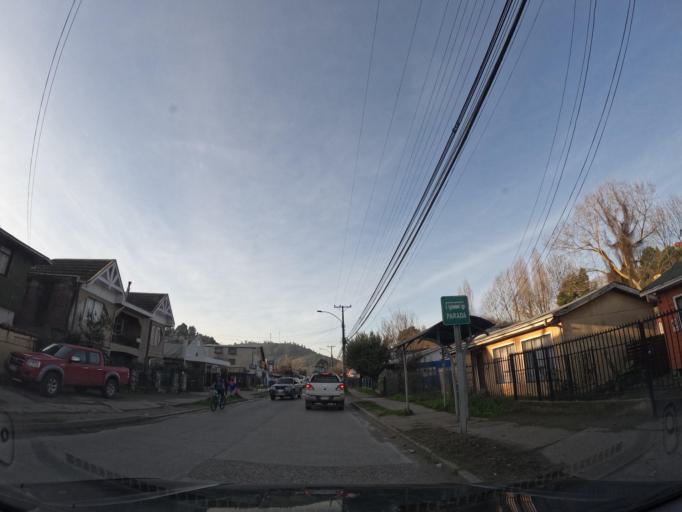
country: CL
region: Biobio
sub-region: Provincia de Concepcion
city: Concepcion
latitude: -36.8375
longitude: -73.0040
